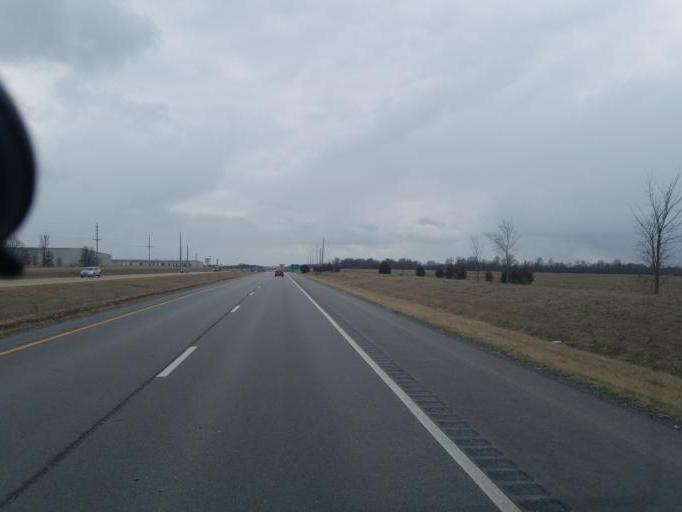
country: US
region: Missouri
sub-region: Randolph County
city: Moberly
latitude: 39.4031
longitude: -92.4127
